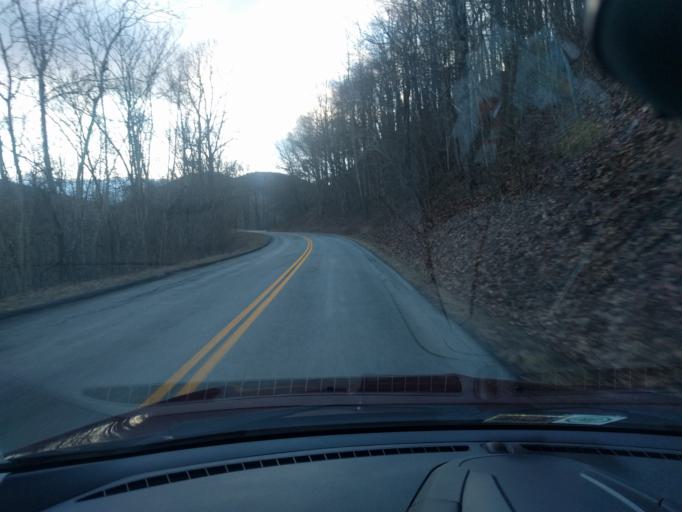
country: US
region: Virginia
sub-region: Botetourt County
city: Buchanan
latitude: 37.4715
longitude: -79.6397
